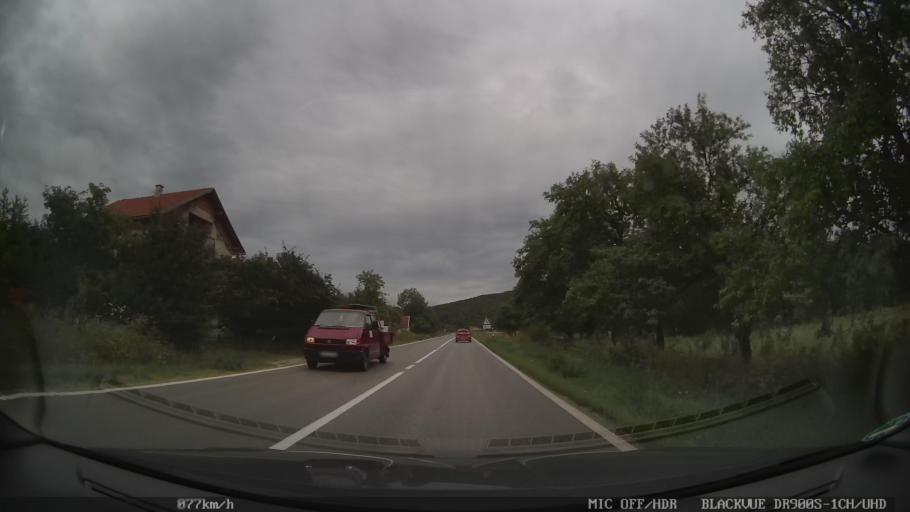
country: HR
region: Licko-Senjska
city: Otocac
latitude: 44.8557
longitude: 15.3323
